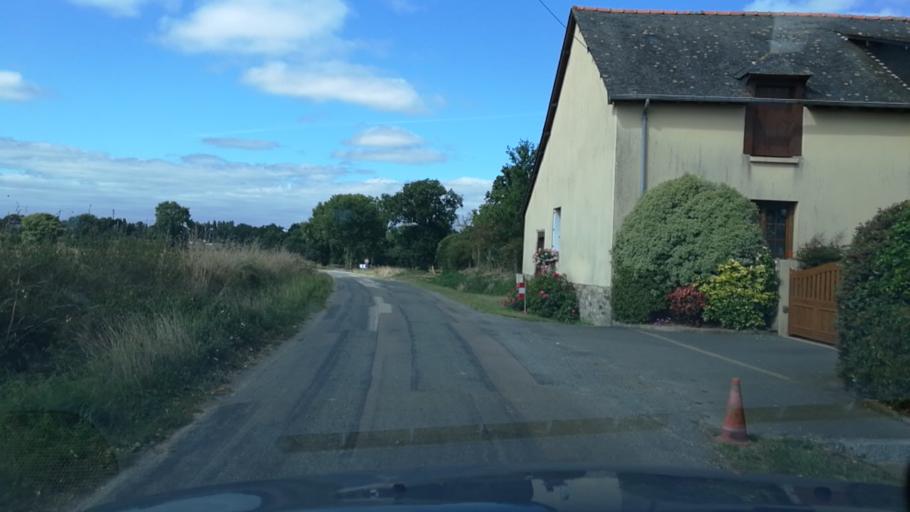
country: FR
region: Brittany
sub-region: Departement d'Ille-et-Vilaine
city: Montgermont
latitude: 48.1458
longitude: -1.7099
